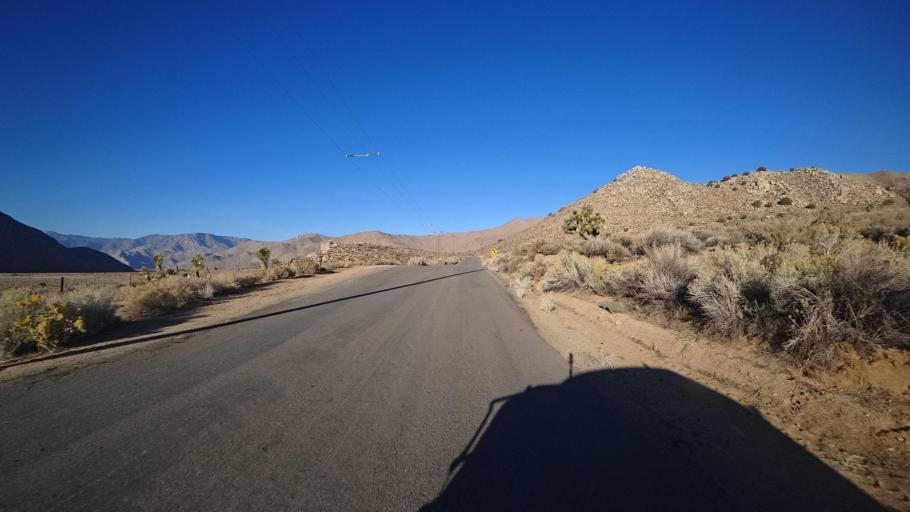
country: US
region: California
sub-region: Kern County
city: Weldon
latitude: 35.5890
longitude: -118.2418
